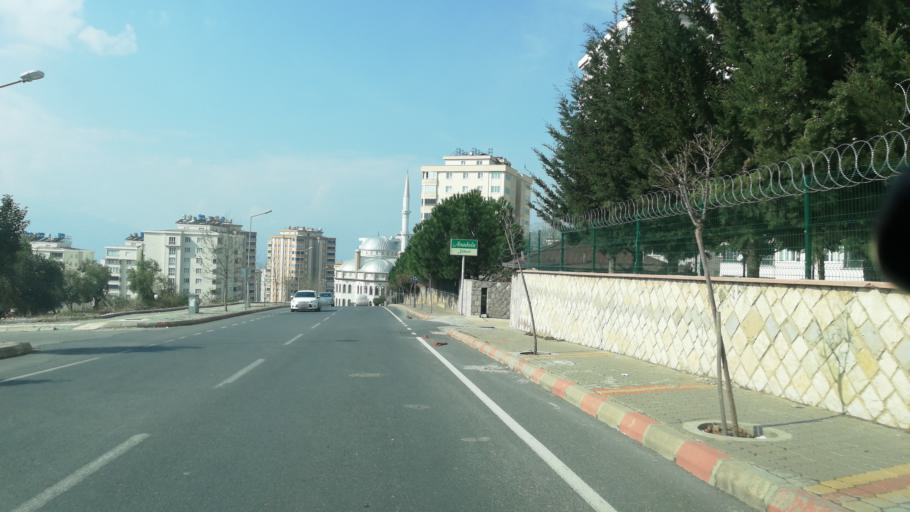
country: TR
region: Kahramanmaras
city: Kahramanmaras
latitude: 37.5868
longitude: 36.8773
